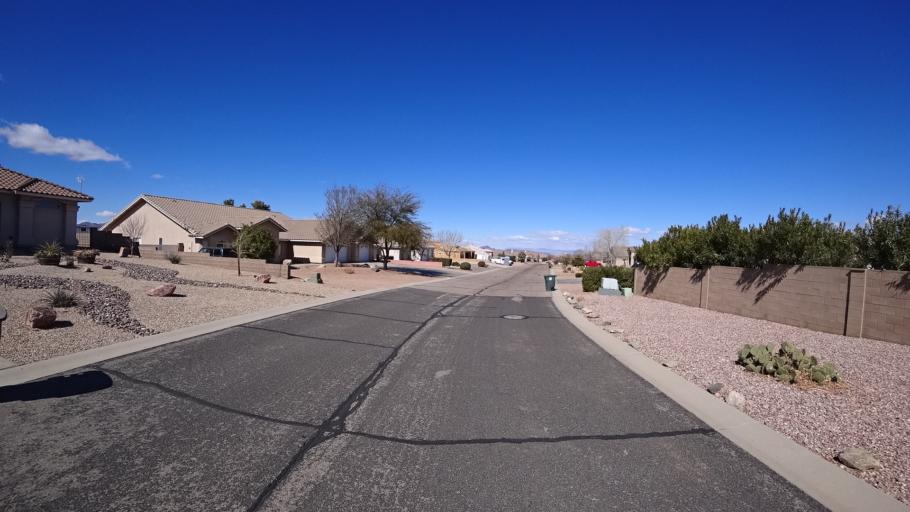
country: US
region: Arizona
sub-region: Mohave County
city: Kingman
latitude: 35.2078
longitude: -113.9739
